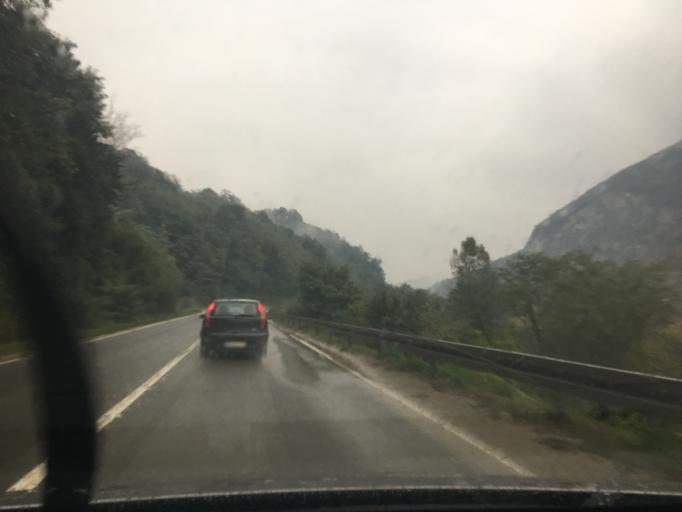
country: RS
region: Central Serbia
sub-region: Pcinjski Okrug
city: Vladicin Han
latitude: 42.7546
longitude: 22.0821
